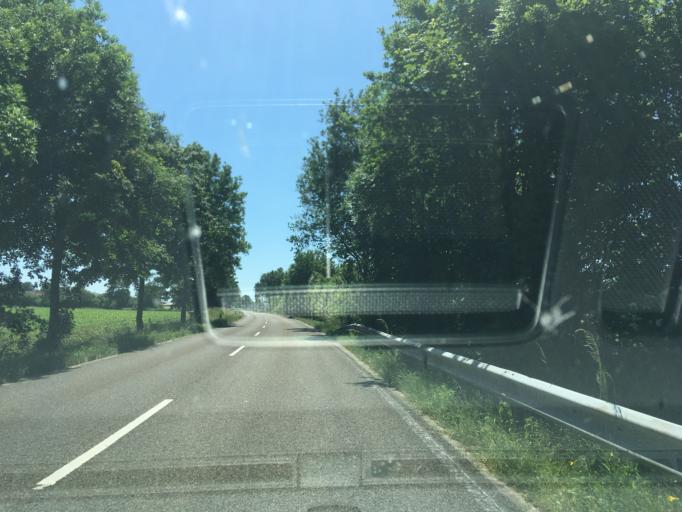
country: DE
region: North Rhine-Westphalia
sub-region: Regierungsbezirk Munster
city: Raesfeld
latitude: 51.7903
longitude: 6.8137
